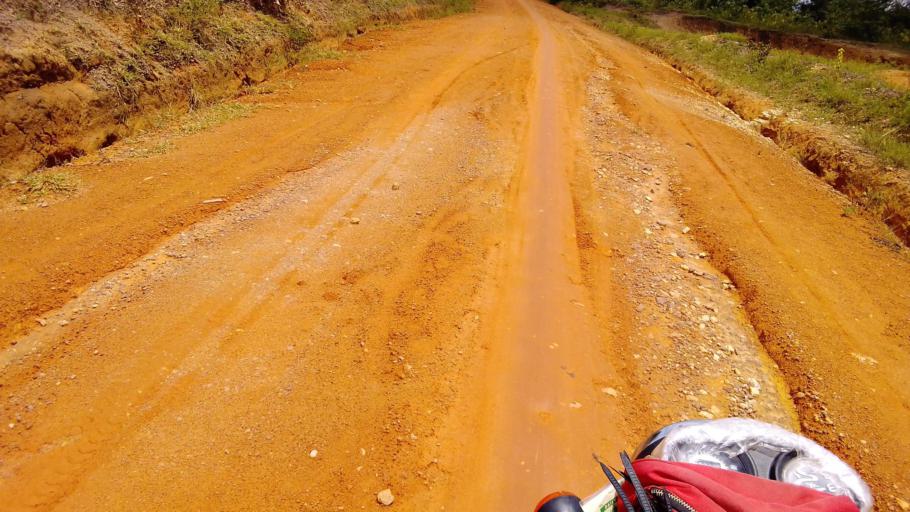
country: SL
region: Eastern Province
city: Koidu
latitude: 8.6923
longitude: -10.9246
